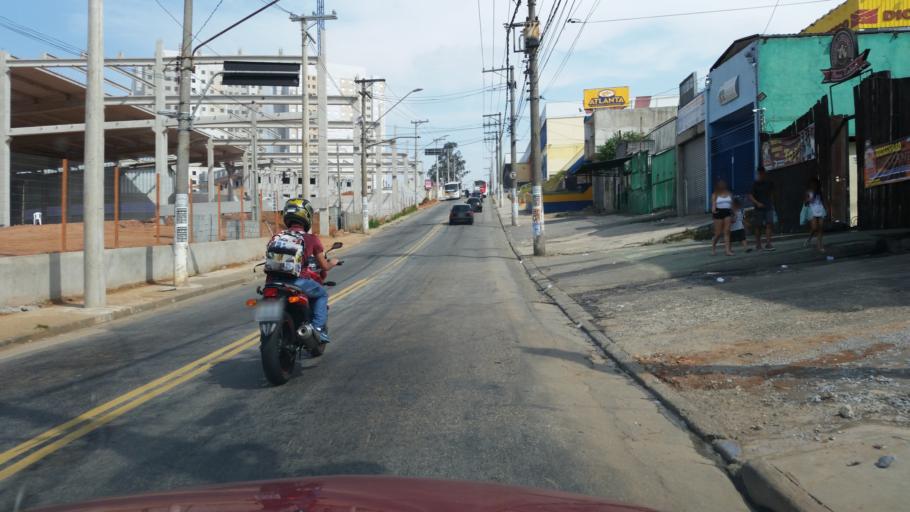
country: BR
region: Sao Paulo
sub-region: Ferraz De Vasconcelos
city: Ferraz de Vasconcelos
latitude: -23.5354
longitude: -46.4283
